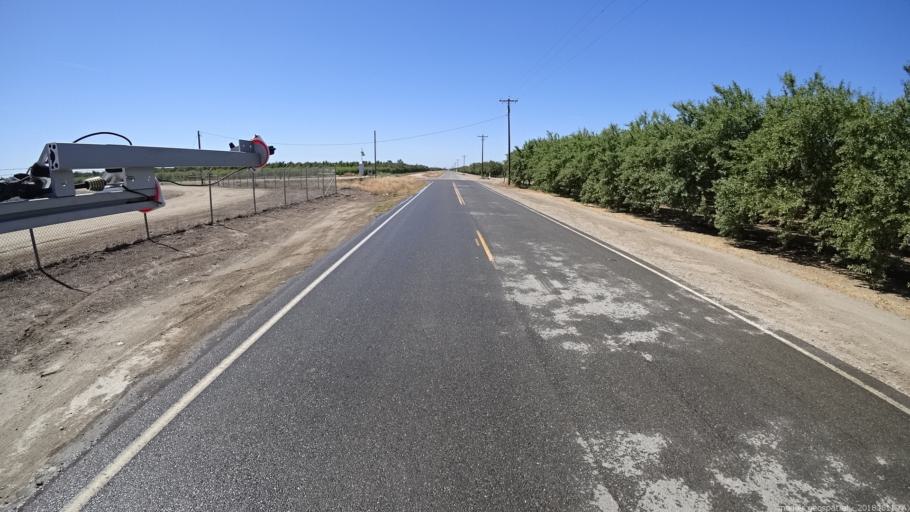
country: US
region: California
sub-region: Madera County
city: Fairmead
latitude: 37.0625
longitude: -120.2024
